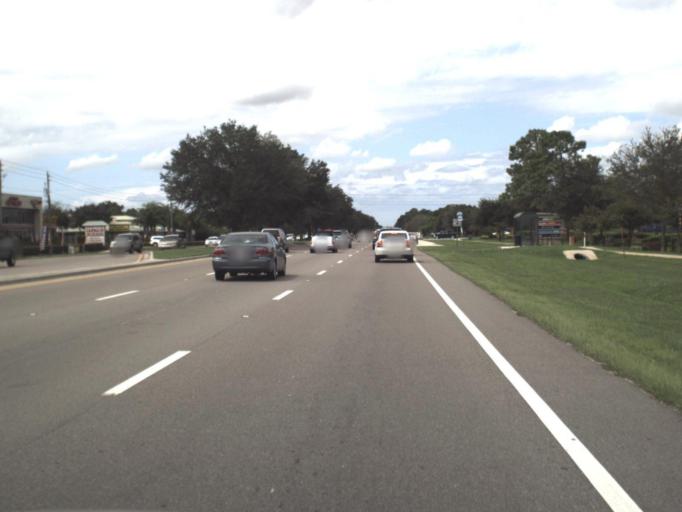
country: US
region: Florida
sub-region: Sarasota County
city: The Meadows
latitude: 27.3884
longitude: -82.4652
